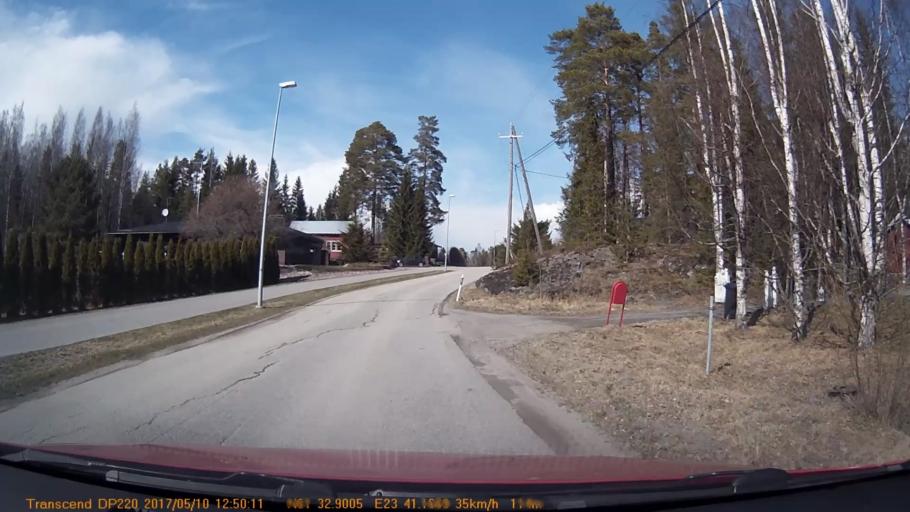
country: FI
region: Pirkanmaa
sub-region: Tampere
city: Yloejaervi
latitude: 61.5484
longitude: 23.6861
